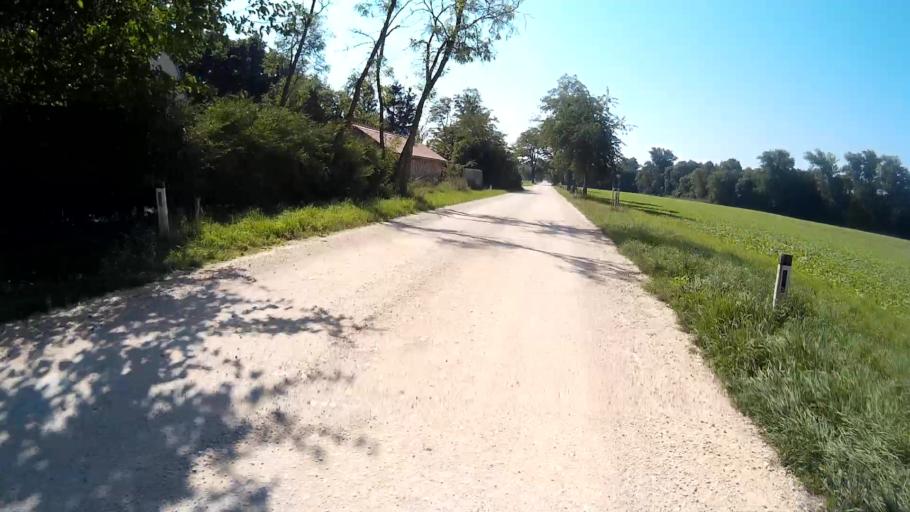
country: CZ
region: South Moravian
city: Novosedly
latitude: 48.7995
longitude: 16.4929
